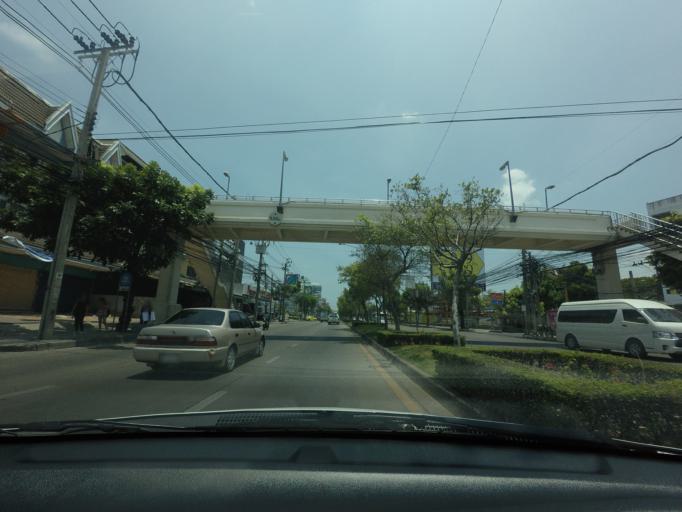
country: TH
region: Bangkok
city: Khan Na Yao
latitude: 13.8302
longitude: 100.6589
